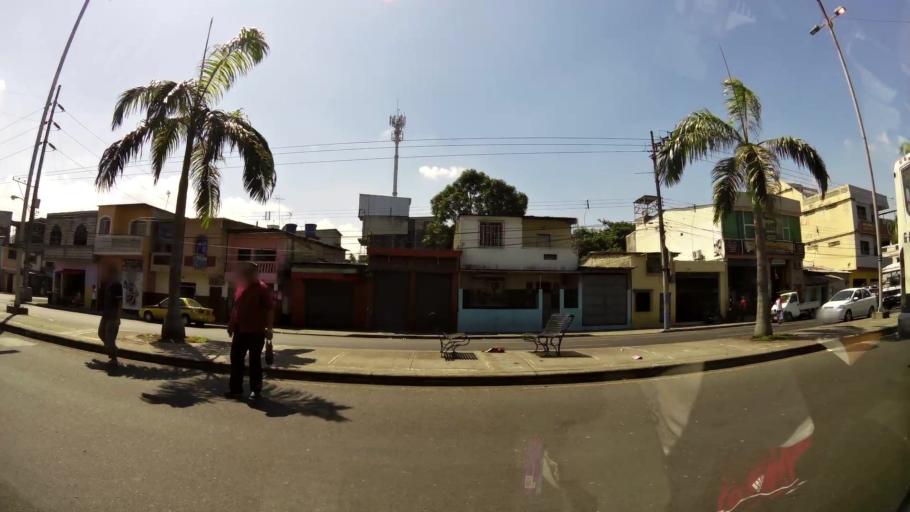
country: EC
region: Guayas
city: Guayaquil
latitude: -2.1978
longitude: -79.9318
